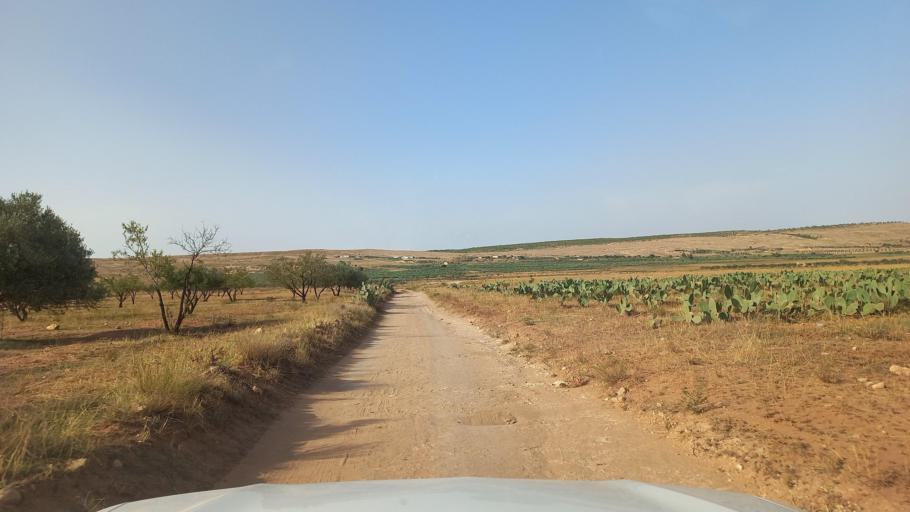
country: TN
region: Al Qasrayn
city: Kasserine
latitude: 35.3509
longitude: 8.8485
